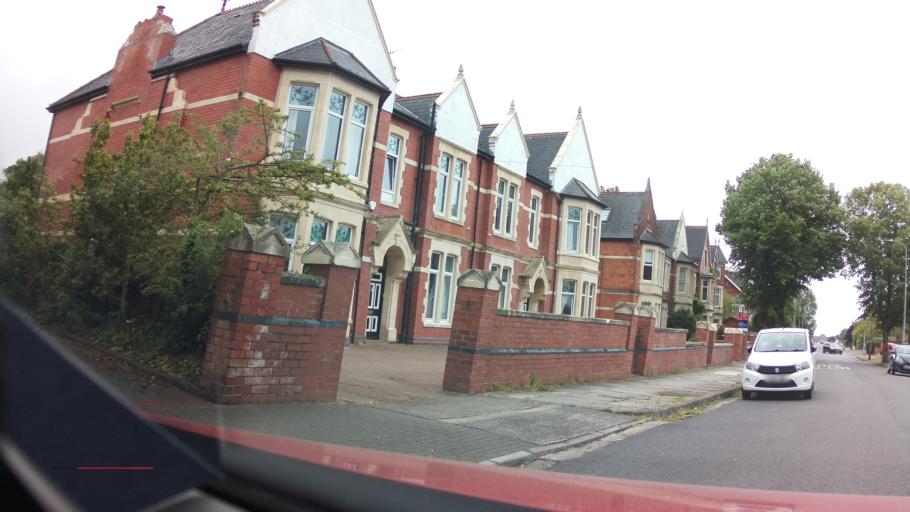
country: GB
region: Wales
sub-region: Vale of Glamorgan
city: Penarth
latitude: 51.4294
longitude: -3.1737
